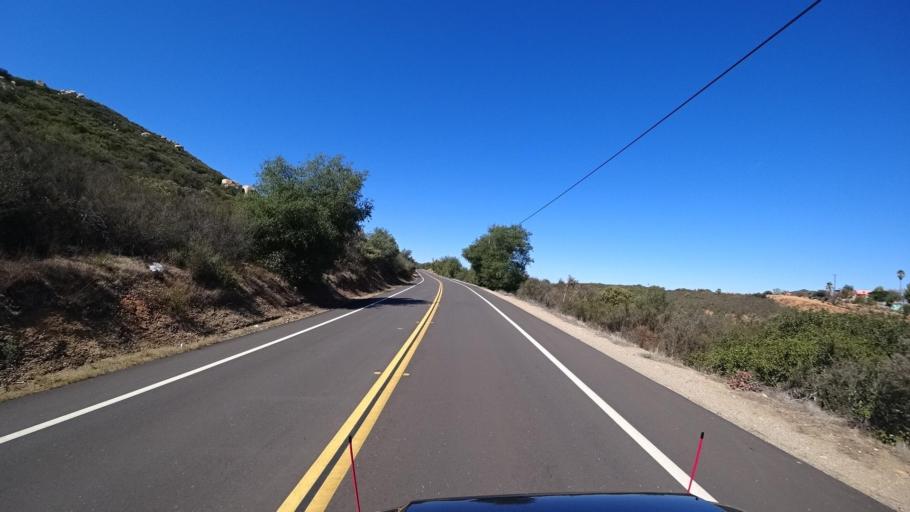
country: US
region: California
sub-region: San Diego County
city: Jamul
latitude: 32.7317
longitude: -116.7898
